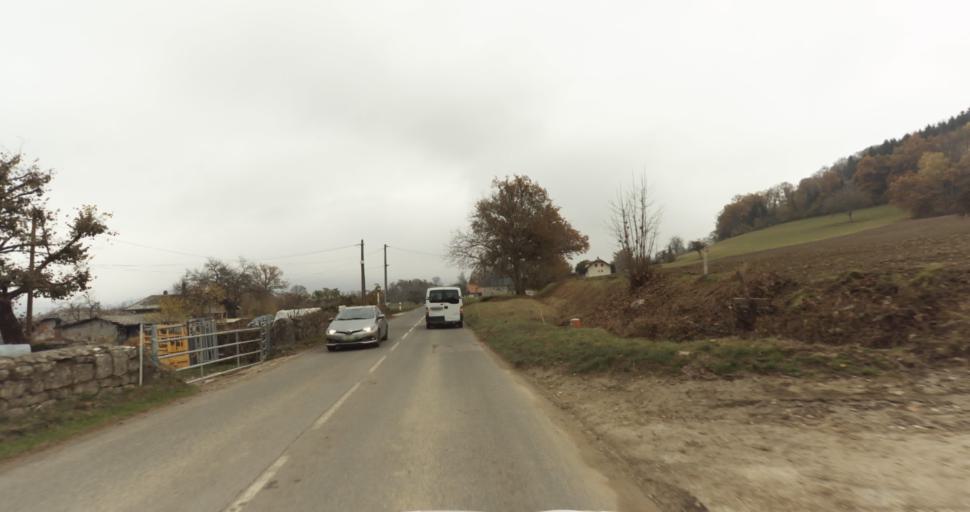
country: FR
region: Rhone-Alpes
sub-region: Departement de la Haute-Savoie
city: Alby-sur-Cheran
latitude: 45.7901
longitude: 6.0117
